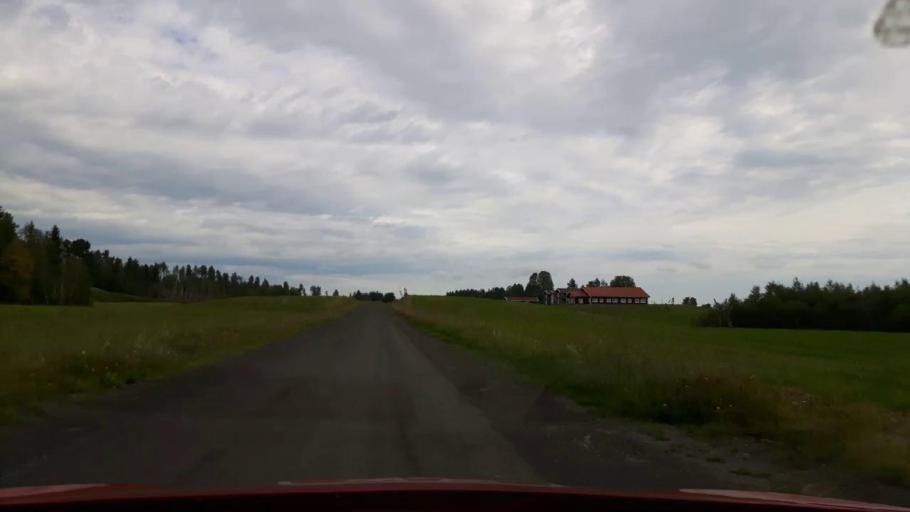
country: SE
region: Jaemtland
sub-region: OEstersunds Kommun
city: Lit
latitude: 63.4131
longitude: 15.2448
